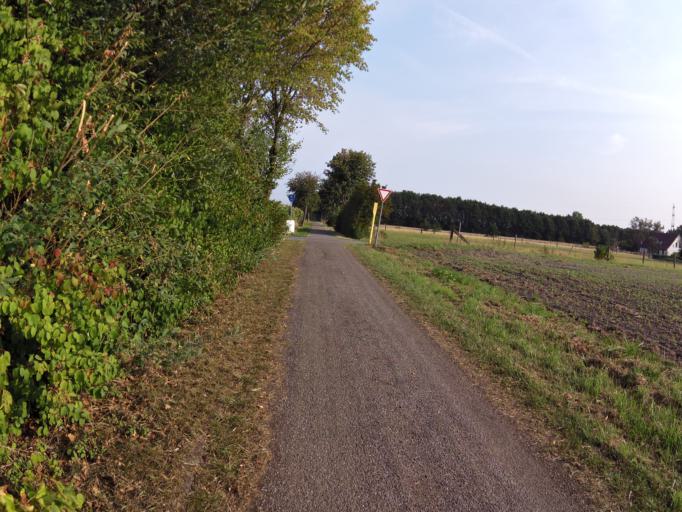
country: DE
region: North Rhine-Westphalia
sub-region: Regierungsbezirk Detmold
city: Petershagen
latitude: 52.3959
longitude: 8.9643
